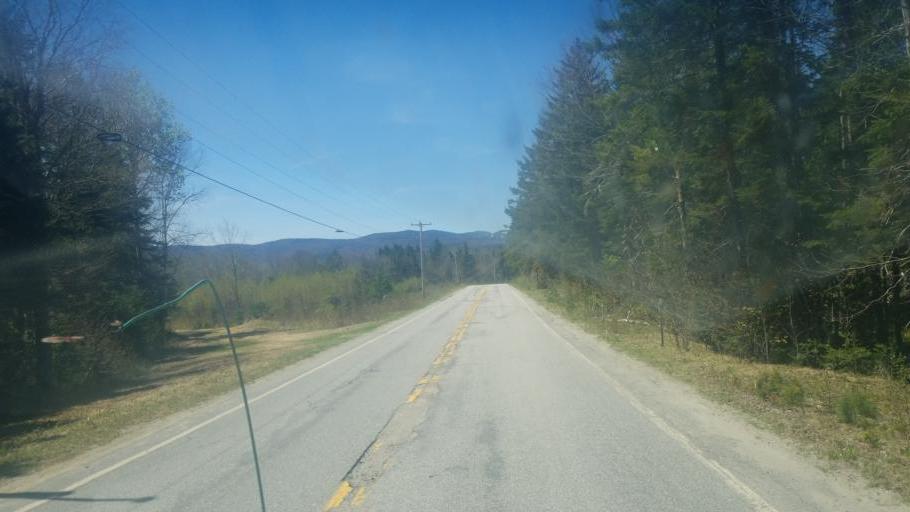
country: US
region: New Hampshire
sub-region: Coos County
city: Jefferson
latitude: 44.2584
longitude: -71.3923
